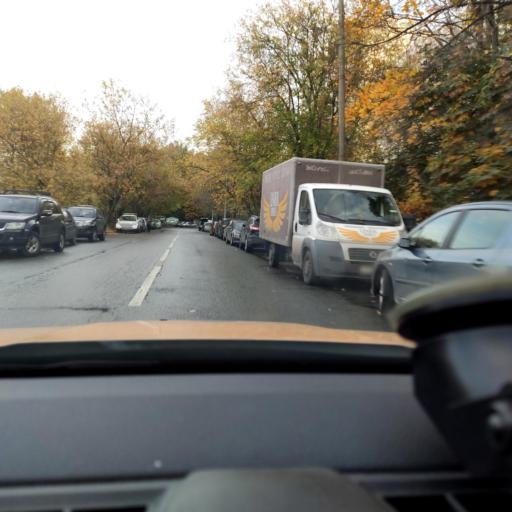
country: RU
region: Moscow
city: Vatutino
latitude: 55.8568
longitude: 37.6873
